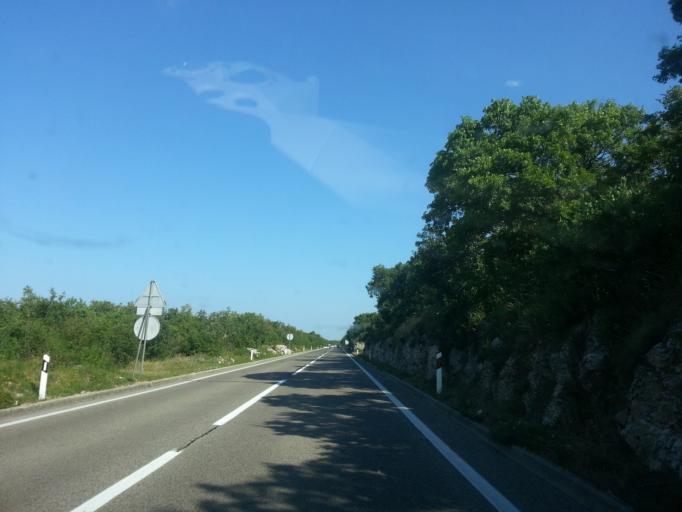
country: HR
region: Primorsko-Goranska
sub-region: Grad Crikvenica
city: Jadranovo
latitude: 45.2457
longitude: 14.6070
